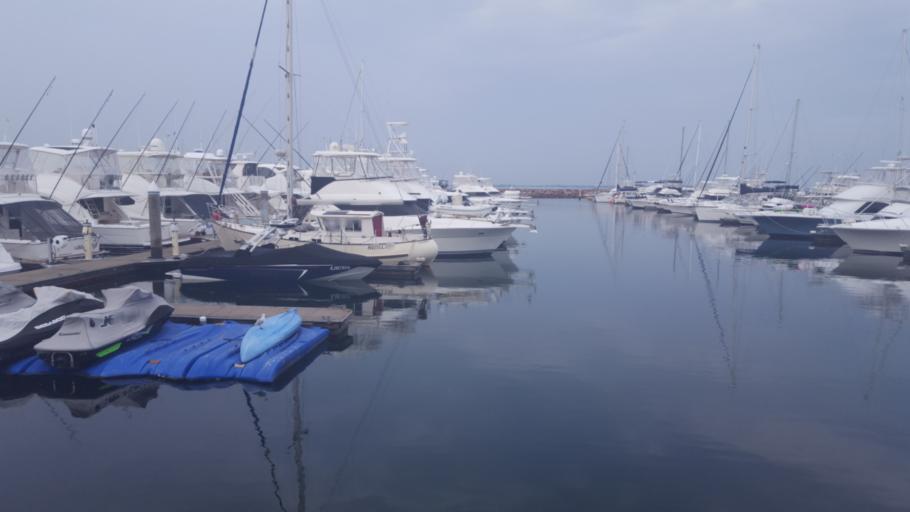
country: AU
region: New South Wales
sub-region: Port Stephens Shire
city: Nelson Bay
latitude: -32.7194
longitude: 152.1443
